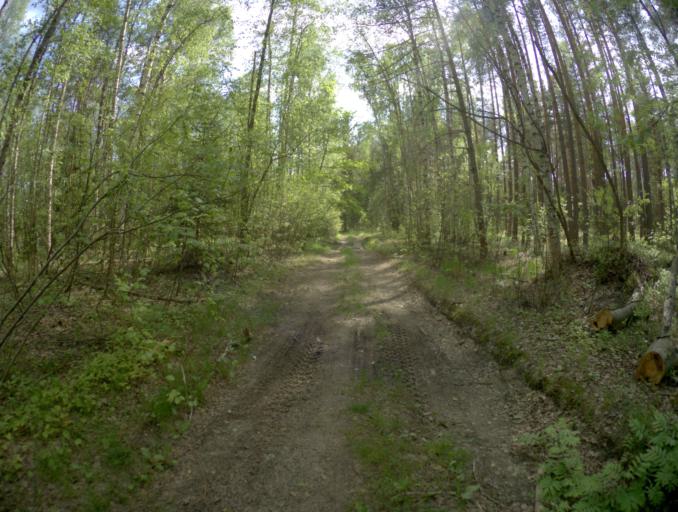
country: RU
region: Vladimir
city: Ivanishchi
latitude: 55.6732
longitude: 40.3932
